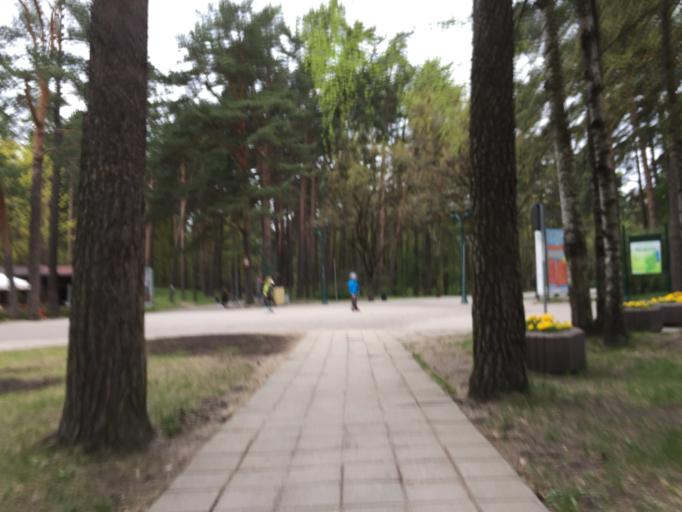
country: LV
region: Riga
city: Jaunciems
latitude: 57.0059
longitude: 24.1572
